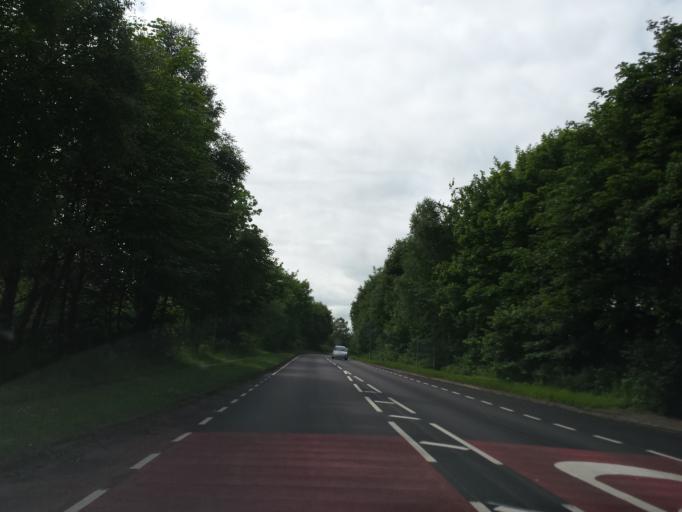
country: GB
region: Scotland
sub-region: Highland
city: Fort William
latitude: 56.8431
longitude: -5.1430
